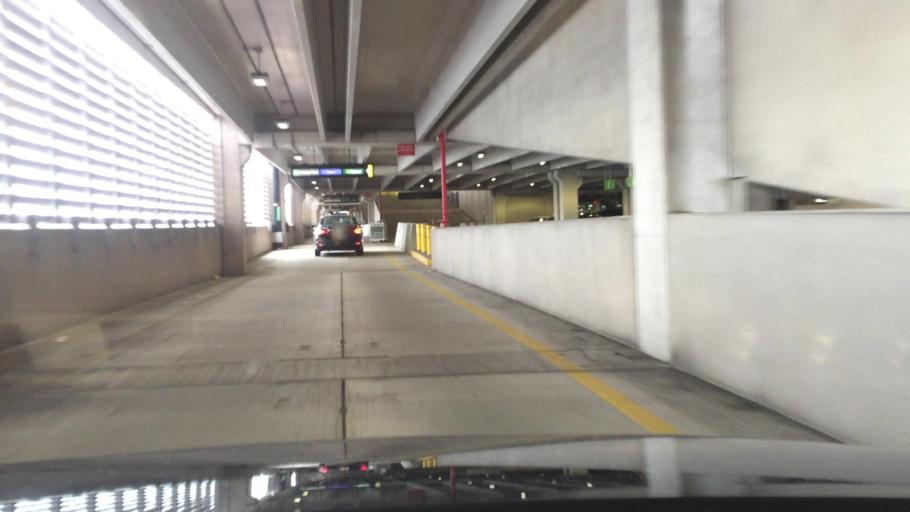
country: US
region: Massachusetts
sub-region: Suffolk County
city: Chelsea
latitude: 42.3679
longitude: -71.0313
